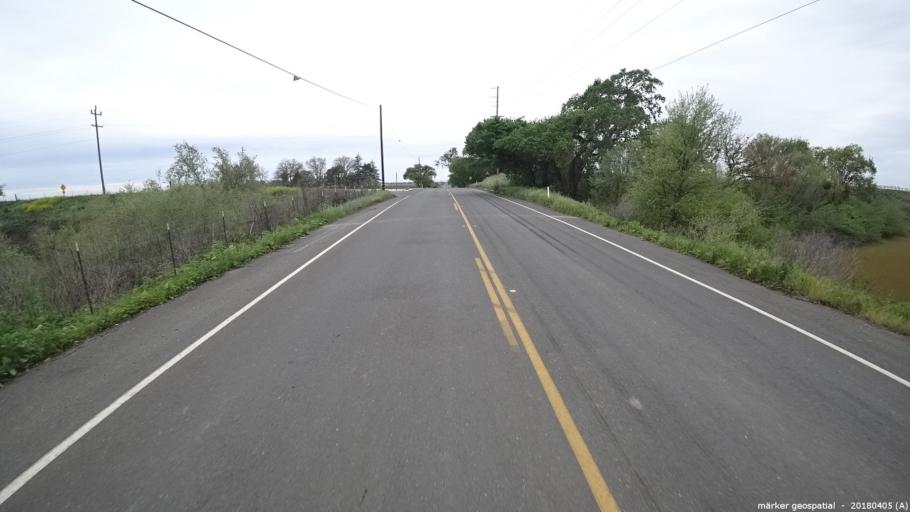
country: US
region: California
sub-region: Sacramento County
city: Walnut Grove
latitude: 38.3205
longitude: -121.5193
